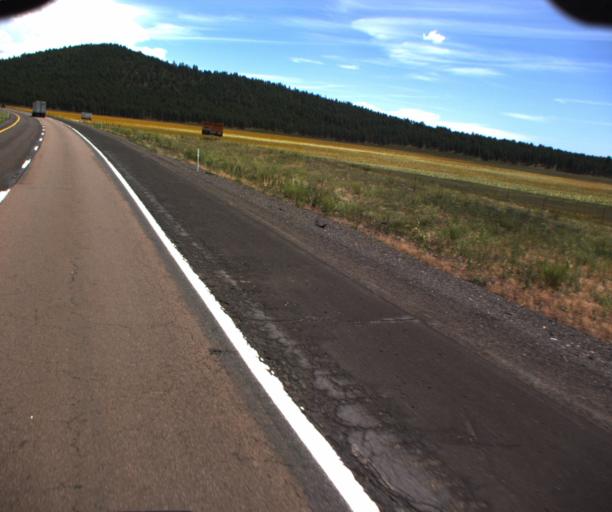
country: US
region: Arizona
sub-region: Coconino County
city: Williams
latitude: 35.2578
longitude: -112.0843
